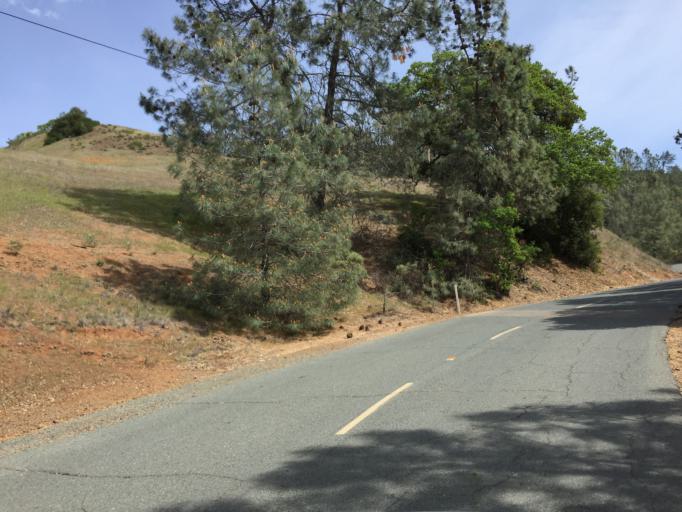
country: US
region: California
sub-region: Contra Costa County
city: Diablo
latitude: 37.8675
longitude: -121.9346
